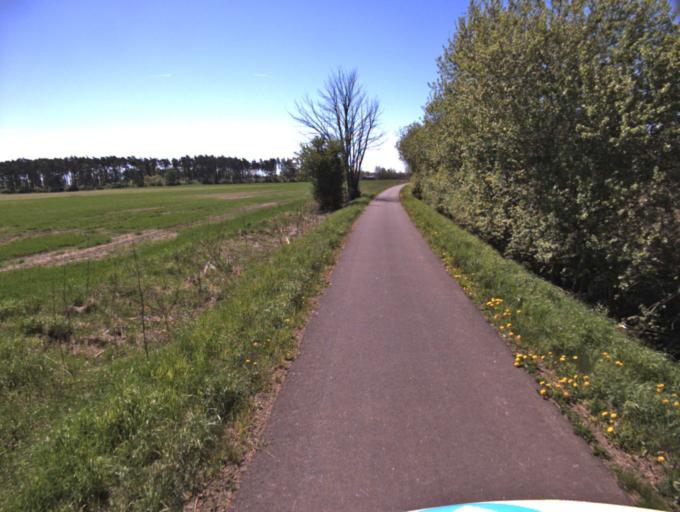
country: SE
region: Skane
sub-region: Kristianstads Kommun
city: Norra Asum
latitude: 55.9558
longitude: 14.1574
